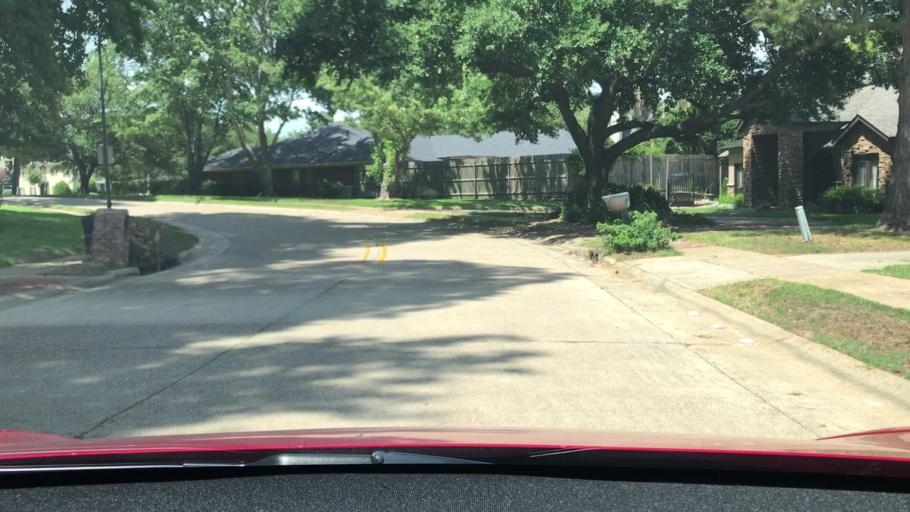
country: US
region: Louisiana
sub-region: Bossier Parish
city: Bossier City
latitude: 32.4244
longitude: -93.7285
